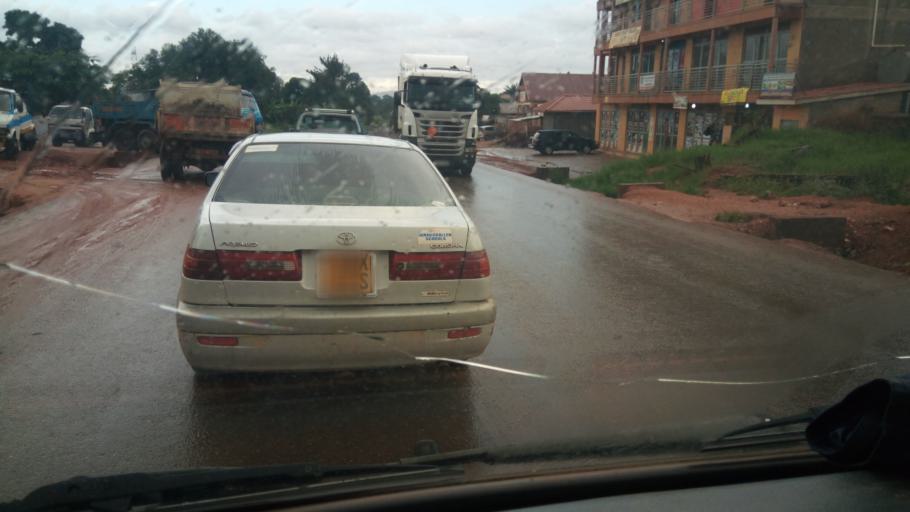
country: UG
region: Central Region
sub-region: Wakiso District
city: Wakiso
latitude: 0.3957
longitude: 32.4976
